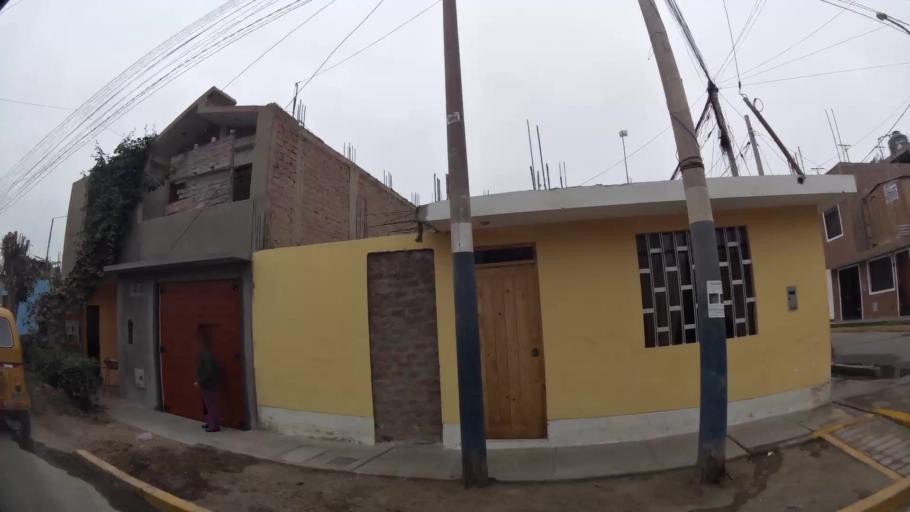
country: PE
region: Ica
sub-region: Provincia de Pisco
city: Pisco
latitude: -13.7059
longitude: -76.2013
